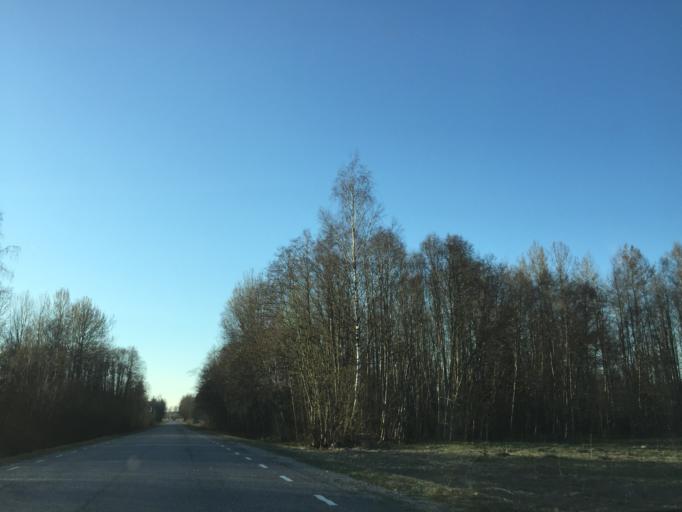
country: EE
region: Ida-Virumaa
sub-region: Sillamaee linn
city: Sillamae
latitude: 59.0887
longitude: 27.6653
